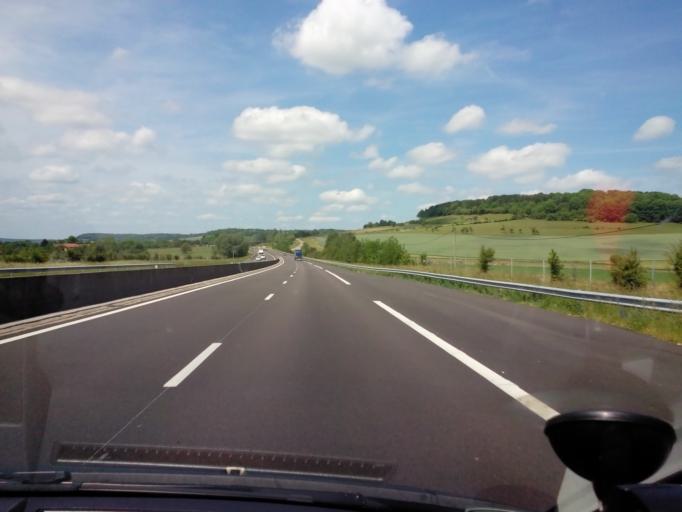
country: FR
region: Champagne-Ardenne
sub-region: Departement de la Haute-Marne
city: Nogent-le-Bas
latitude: 47.9575
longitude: 5.4077
